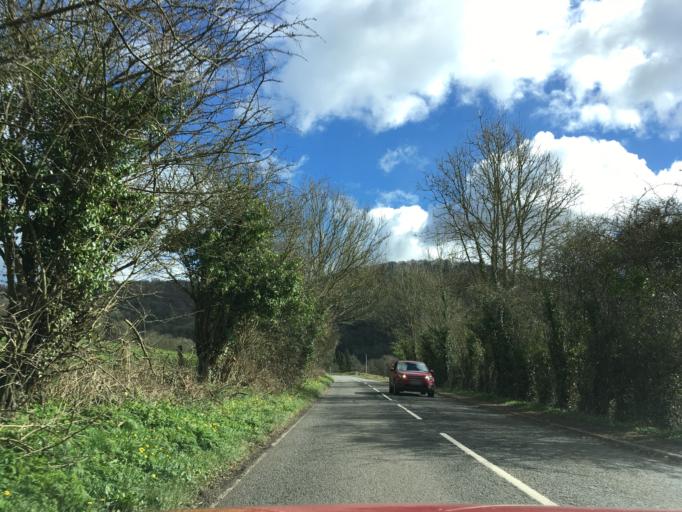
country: GB
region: Wales
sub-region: Monmouthshire
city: Tintern
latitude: 51.7034
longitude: -2.6774
